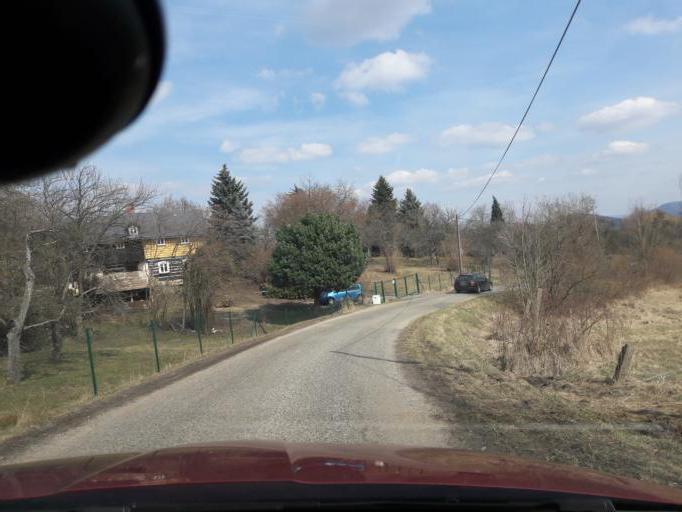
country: CZ
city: Zakupy
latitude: 50.7189
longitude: 14.6124
